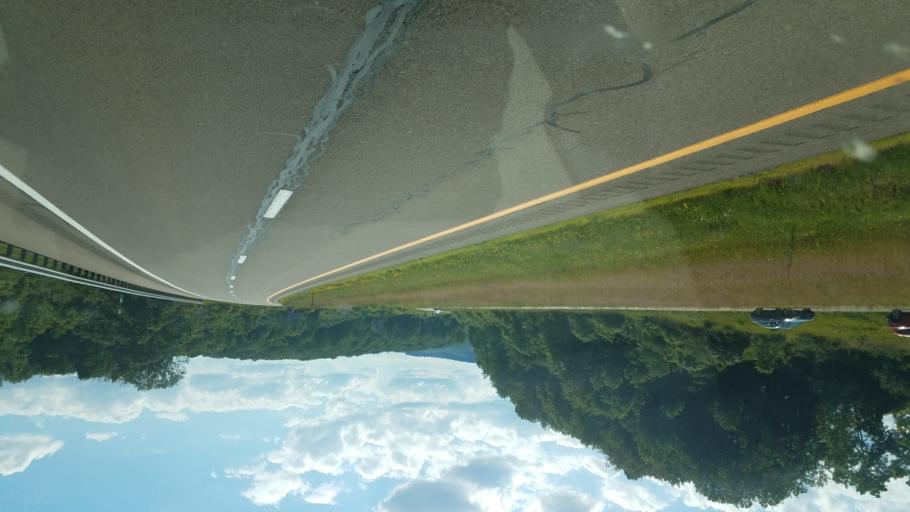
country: US
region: New York
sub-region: Steuben County
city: Hornell
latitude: 42.3800
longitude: -77.6562
